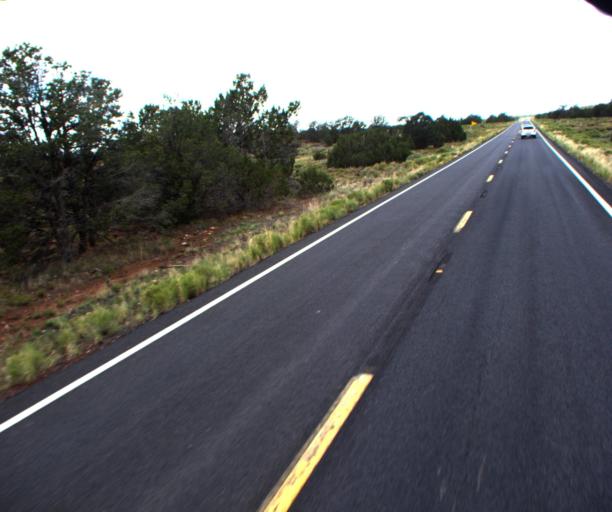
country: US
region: Arizona
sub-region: Coconino County
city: Parks
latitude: 35.5853
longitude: -111.9783
